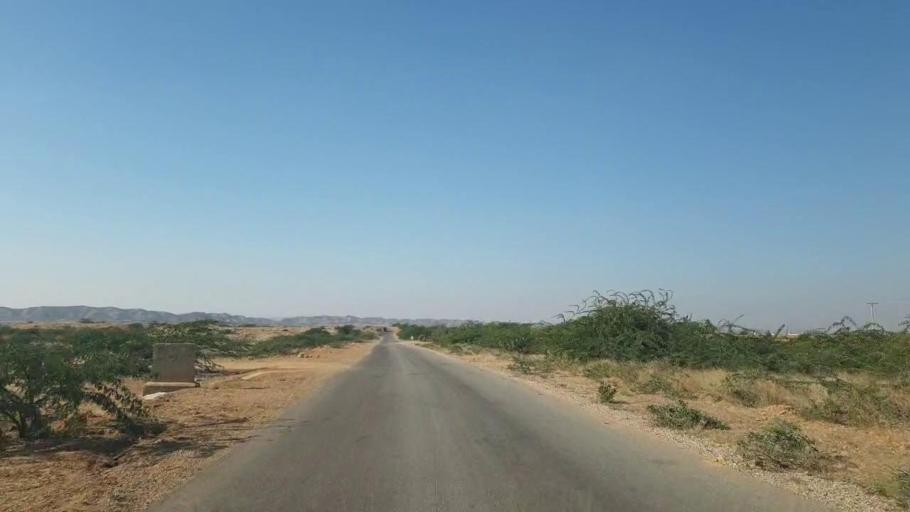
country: PK
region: Sindh
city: Malir Cantonment
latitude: 25.2798
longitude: 67.5849
